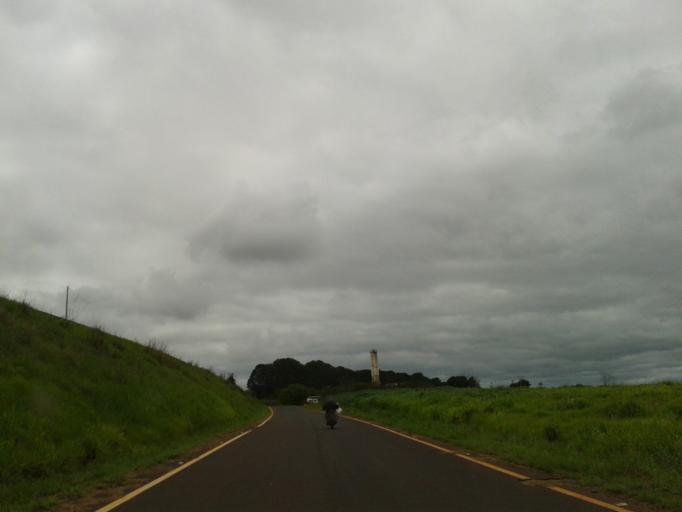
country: BR
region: Minas Gerais
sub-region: Uberlandia
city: Uberlandia
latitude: -18.9381
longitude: -48.2143
